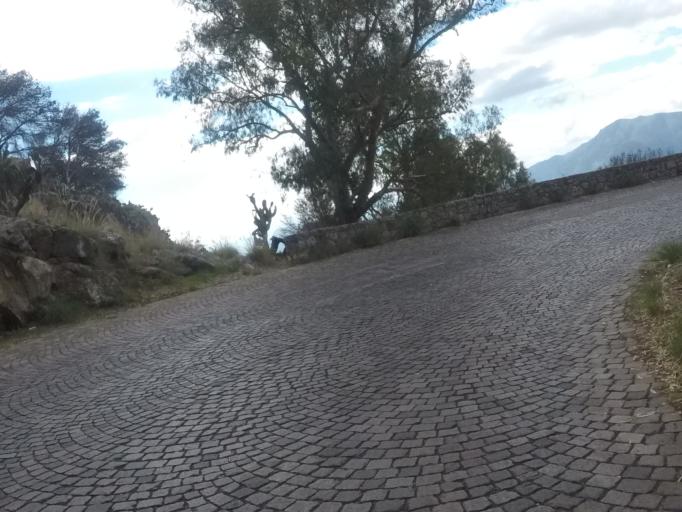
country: IT
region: Sicily
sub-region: Palermo
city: Palermo
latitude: 38.1569
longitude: 13.3610
